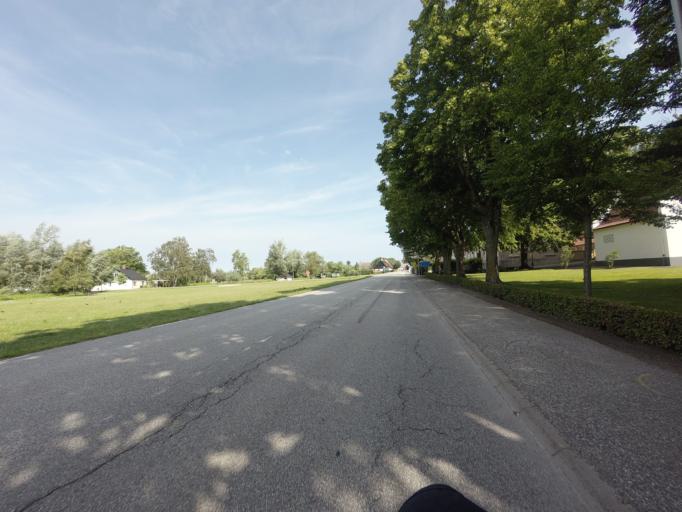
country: SE
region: Skane
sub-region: Vellinge Kommun
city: Vellinge
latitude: 55.5008
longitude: 13.0315
